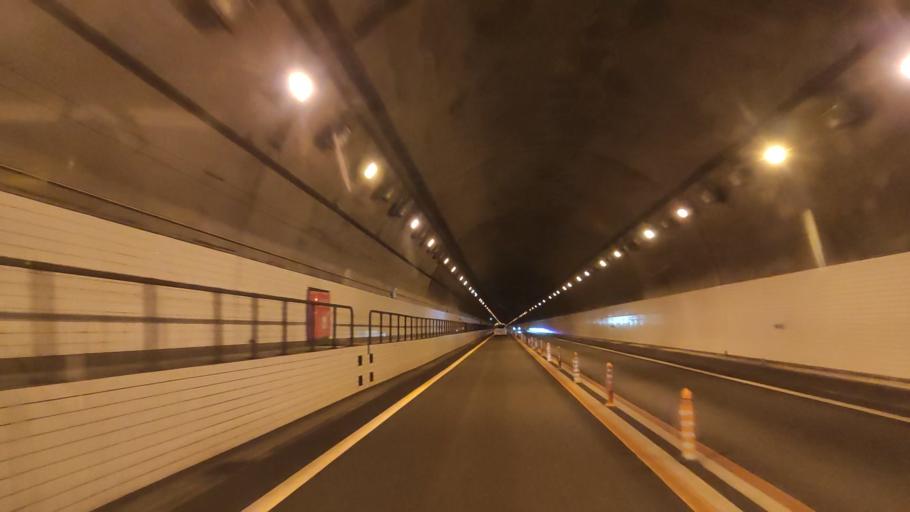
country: JP
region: Ehime
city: Kawanoecho
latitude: 34.0043
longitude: 133.6932
